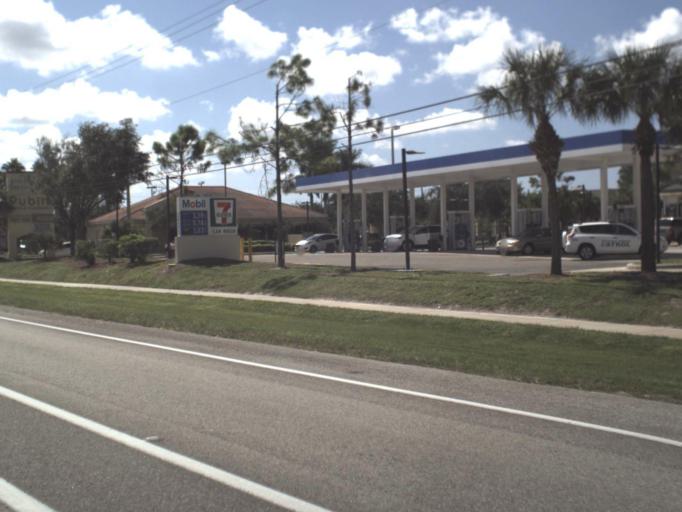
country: US
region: Florida
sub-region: Lee County
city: Bonita Springs
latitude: 26.3838
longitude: -81.8085
